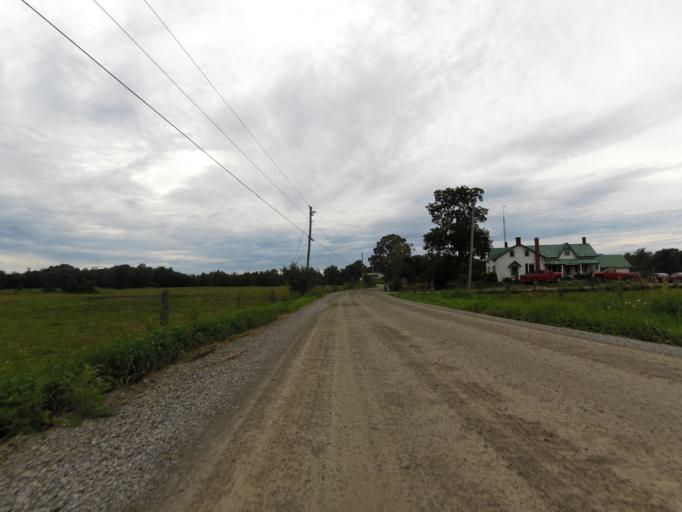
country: CA
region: Ontario
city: Carleton Place
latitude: 45.1570
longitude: -76.1880
